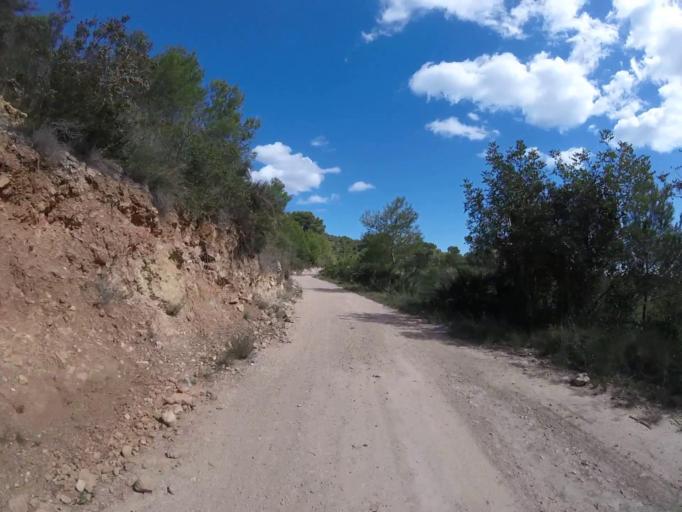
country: ES
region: Valencia
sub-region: Provincia de Castello
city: Santa Magdalena de Pulpis
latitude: 40.3092
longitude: 0.3199
